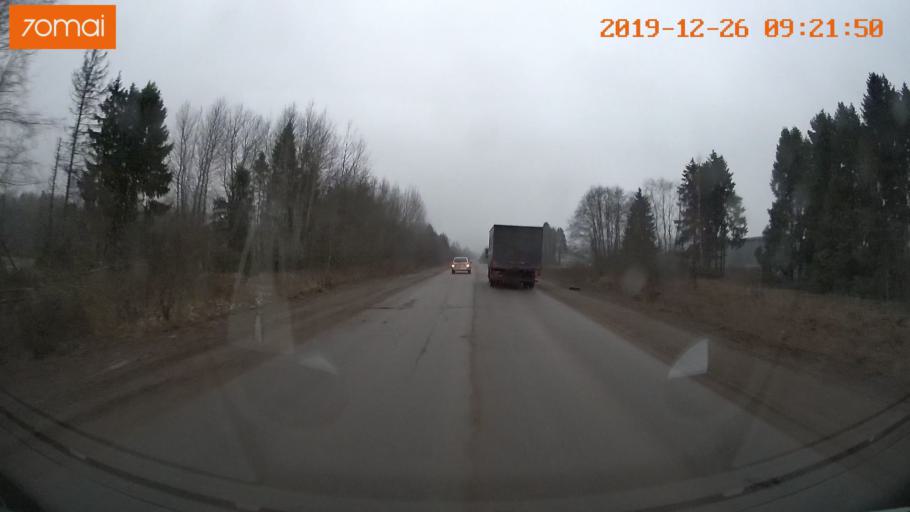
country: RU
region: Vologda
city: Gryazovets
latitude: 58.9731
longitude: 40.2221
